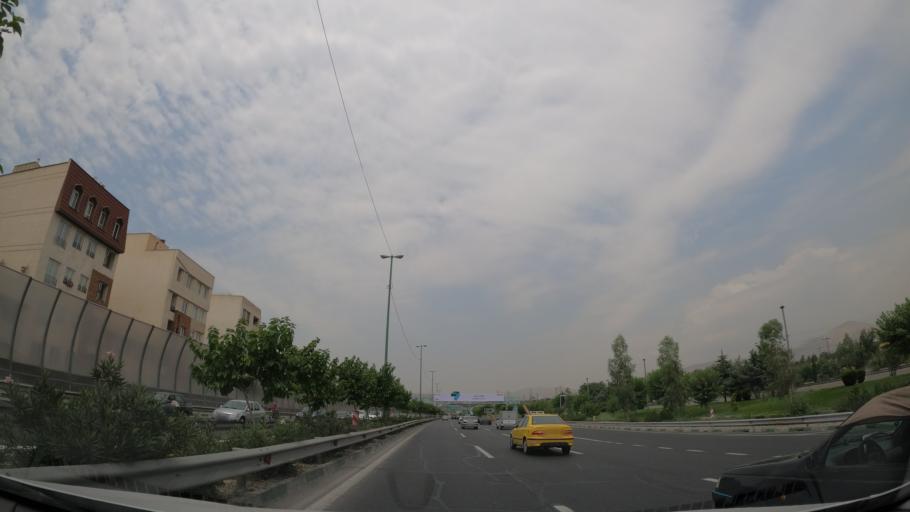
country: IR
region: Tehran
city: Tehran
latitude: 35.7391
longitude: 51.3590
